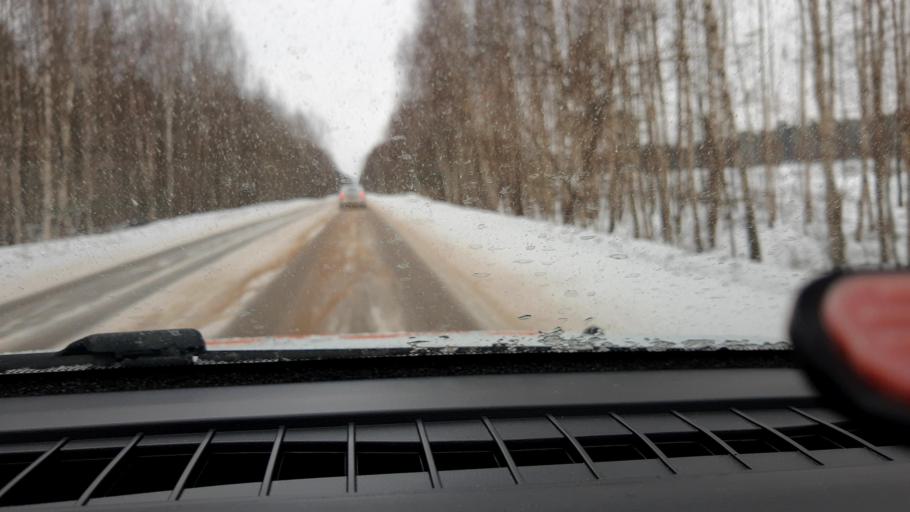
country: RU
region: Nizjnij Novgorod
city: Pamyat' Parizhskoy Kommuny
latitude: 56.2763
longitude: 44.3954
